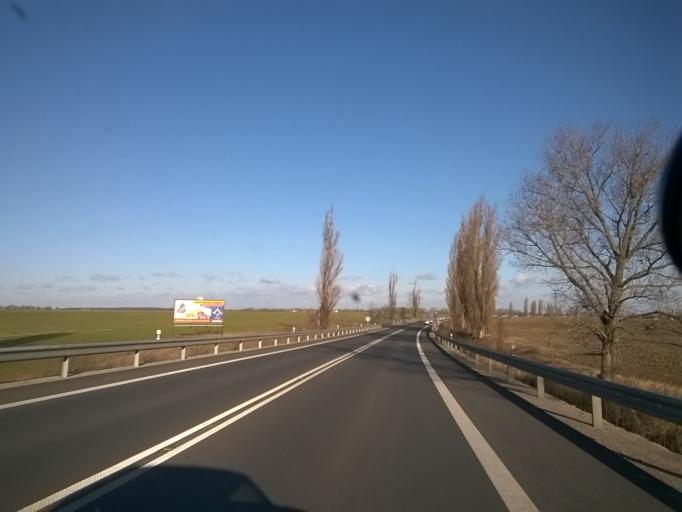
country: SK
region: Trnavsky
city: Sladkovicovo
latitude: 48.2000
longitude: 17.6153
